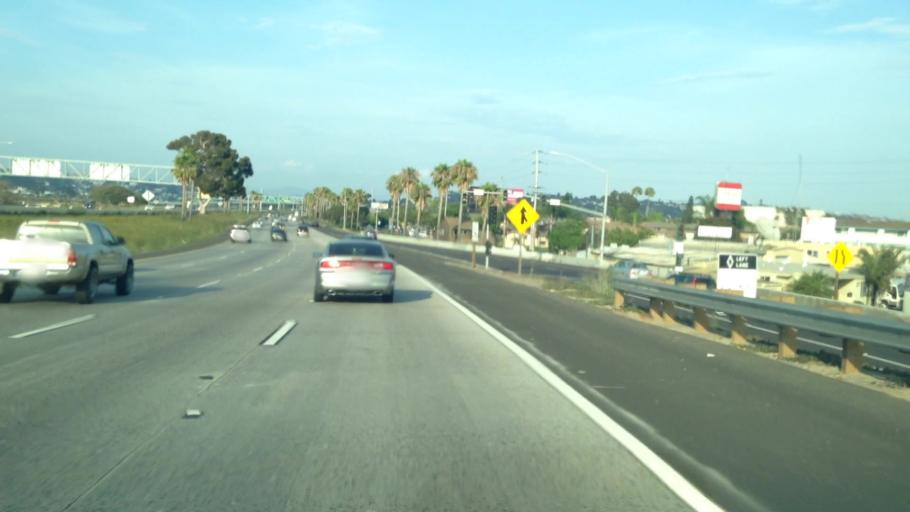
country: US
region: California
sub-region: San Diego County
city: San Diego
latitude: 32.7569
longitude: -117.2208
